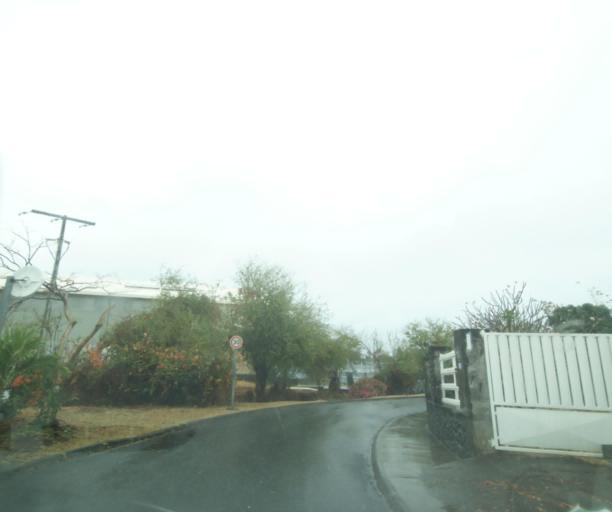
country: RE
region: Reunion
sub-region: Reunion
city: Saint-Paul
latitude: -21.0371
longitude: 55.2220
